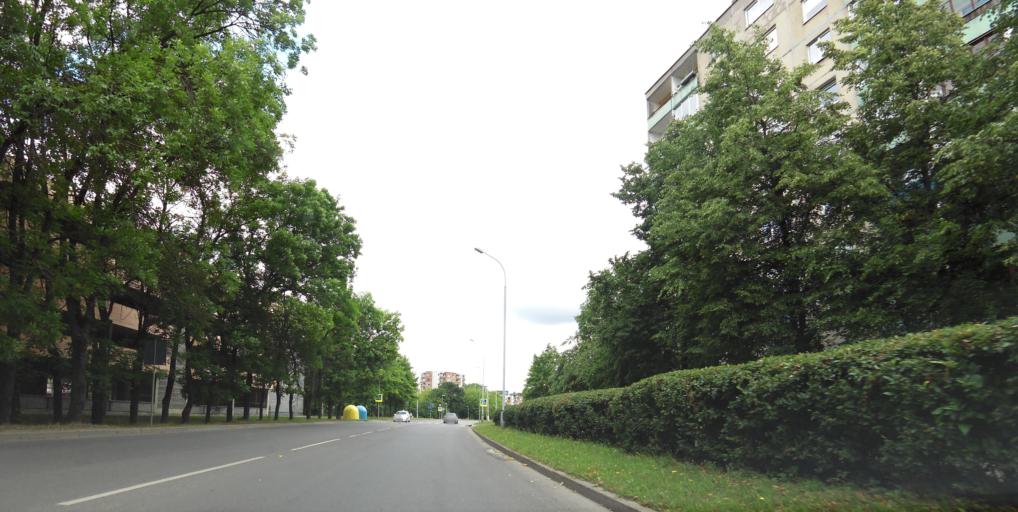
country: LT
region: Vilnius County
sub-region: Vilnius
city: Vilnius
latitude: 54.7012
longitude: 25.2865
